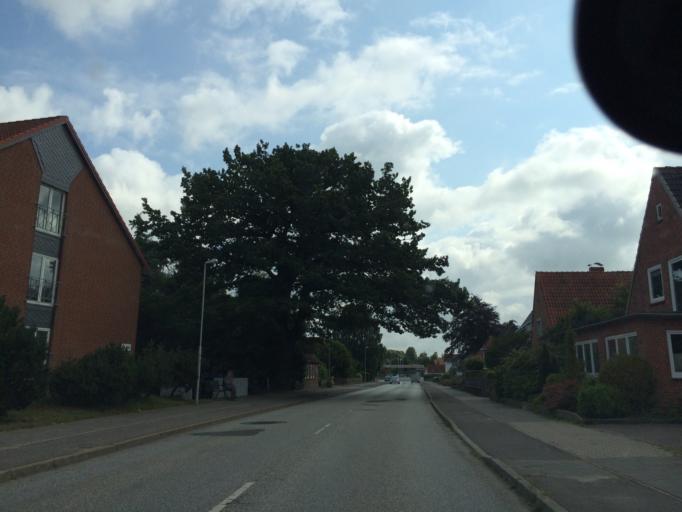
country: DE
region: Schleswig-Holstein
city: Gettorf
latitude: 54.4053
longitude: 9.9676
